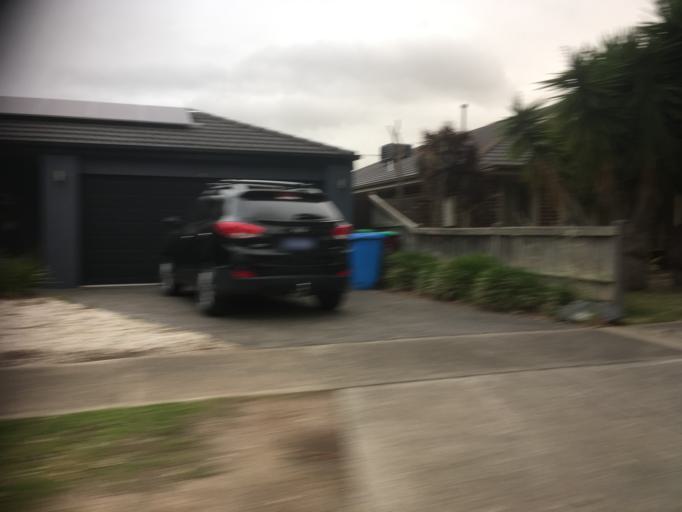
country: AU
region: Victoria
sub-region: Casey
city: Narre Warren South
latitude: -38.0711
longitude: 145.3181
